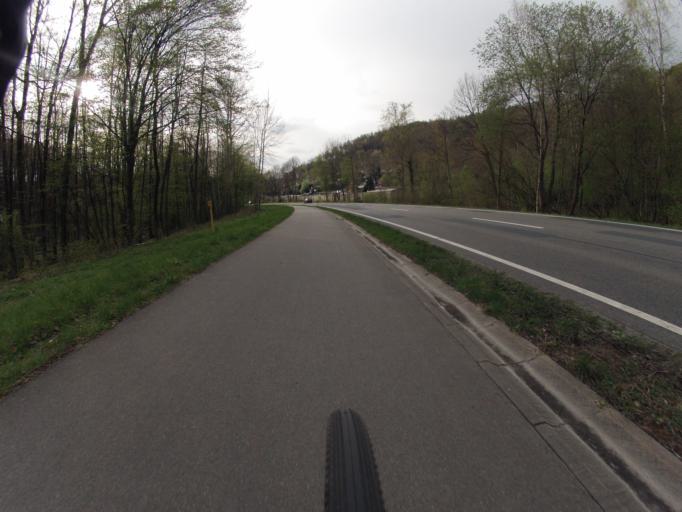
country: DE
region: North Rhine-Westphalia
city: Ibbenburen
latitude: 52.2338
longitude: 7.7493
